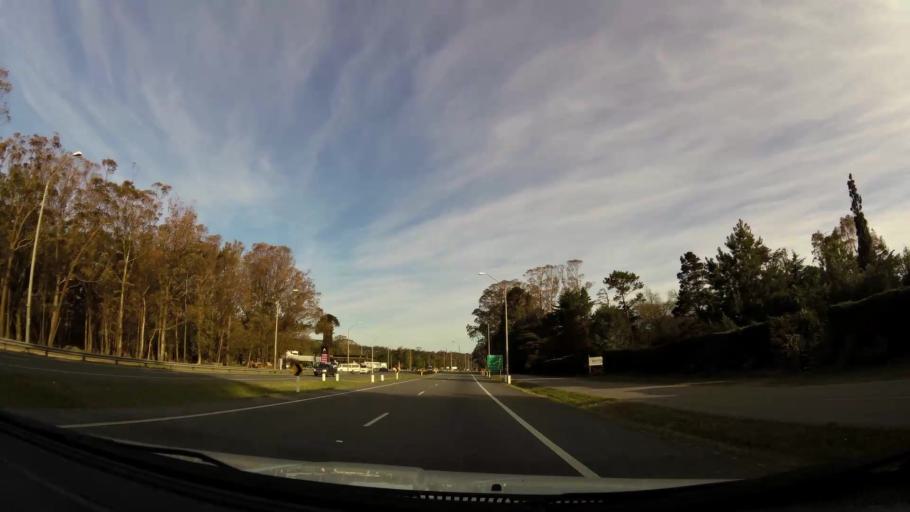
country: UY
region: Maldonado
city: Maldonado
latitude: -34.8785
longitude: -55.0546
